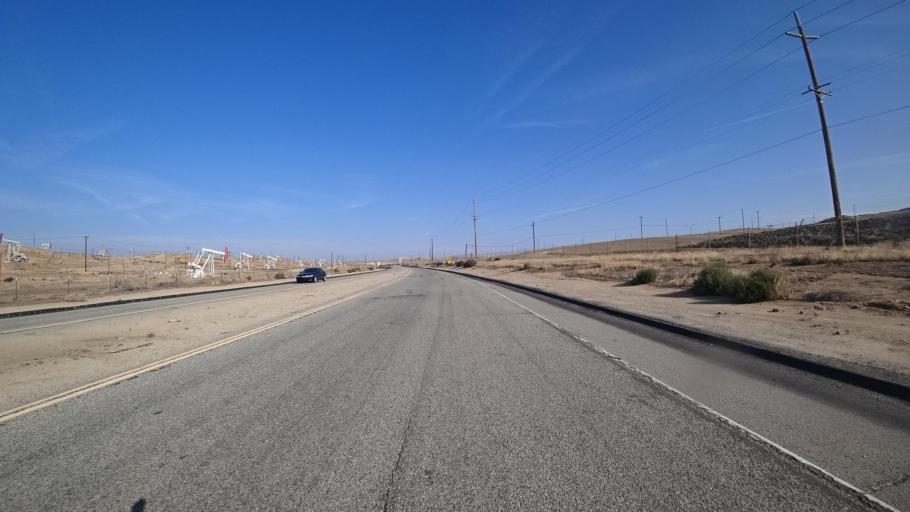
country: US
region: California
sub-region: Kern County
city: Oildale
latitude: 35.4644
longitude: -119.0256
